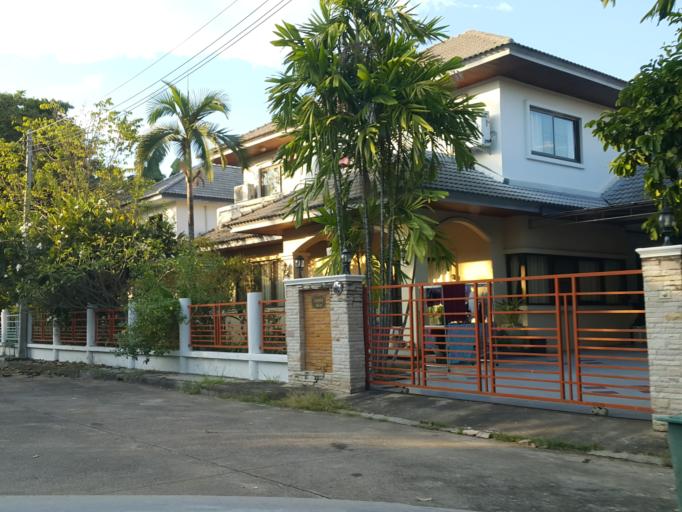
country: TH
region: Chiang Mai
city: San Kamphaeng
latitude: 18.7615
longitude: 99.0736
